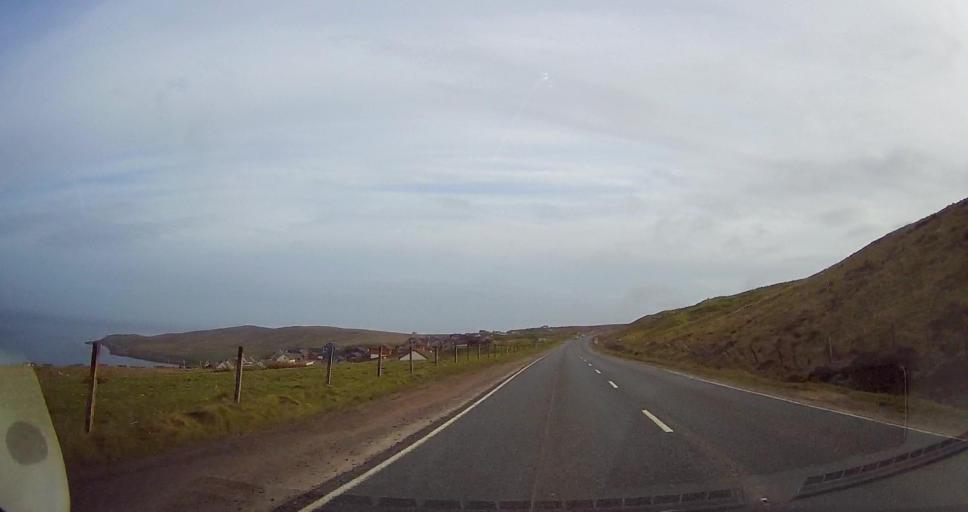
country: GB
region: Scotland
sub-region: Shetland Islands
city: Lerwick
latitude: 60.1326
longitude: -1.2146
